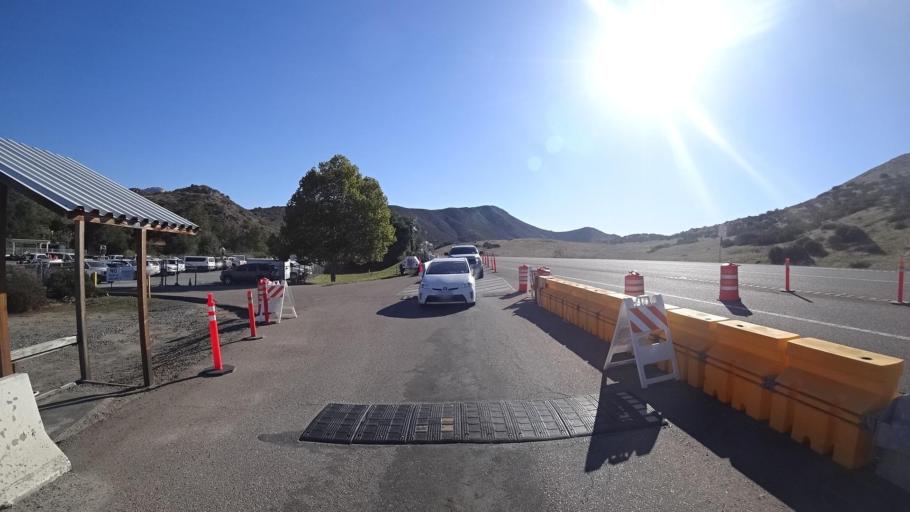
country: US
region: California
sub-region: San Diego County
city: Jamul
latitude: 32.6641
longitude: -116.8184
